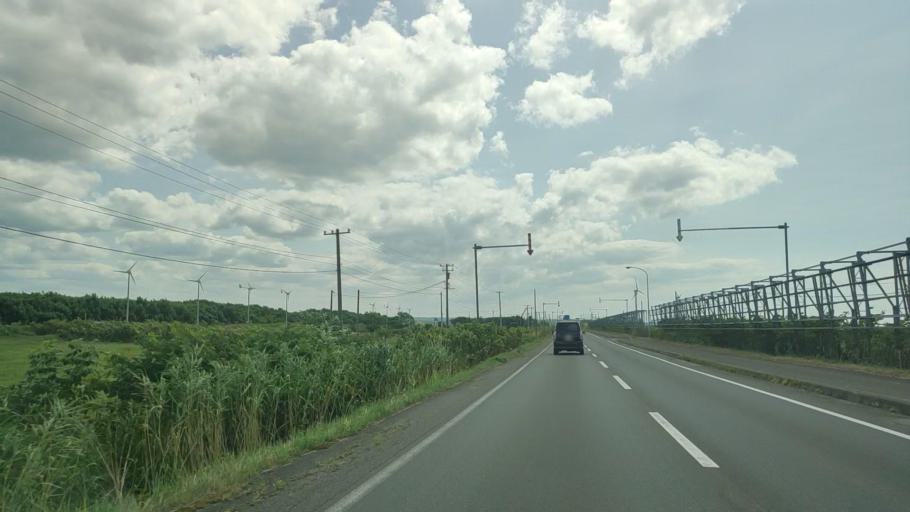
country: JP
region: Hokkaido
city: Makubetsu
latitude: 44.7596
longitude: 141.7942
